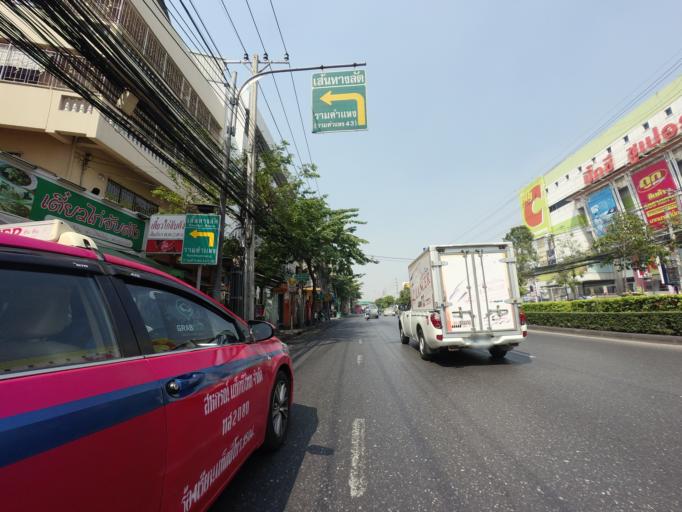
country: TH
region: Bangkok
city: Wang Thonglang
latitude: 13.7845
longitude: 100.6120
